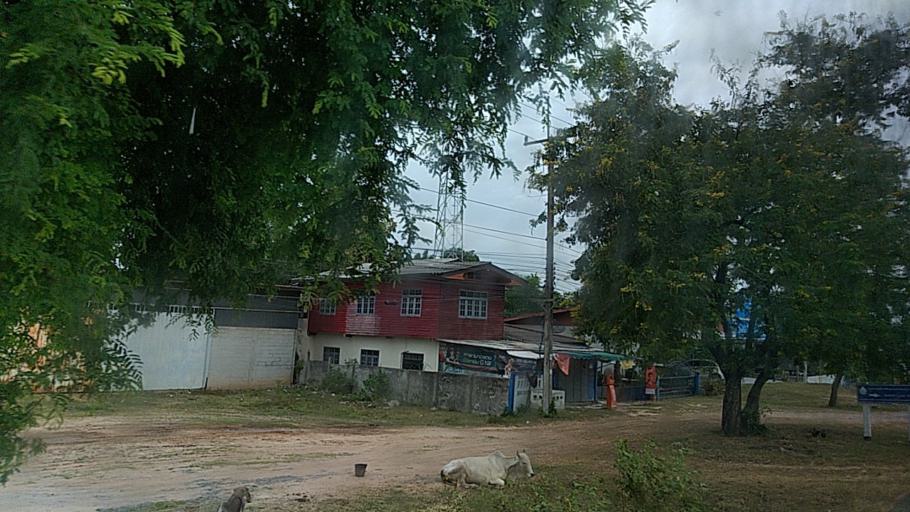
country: TH
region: Kalasin
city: Khong Chai
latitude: 16.1386
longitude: 103.4369
